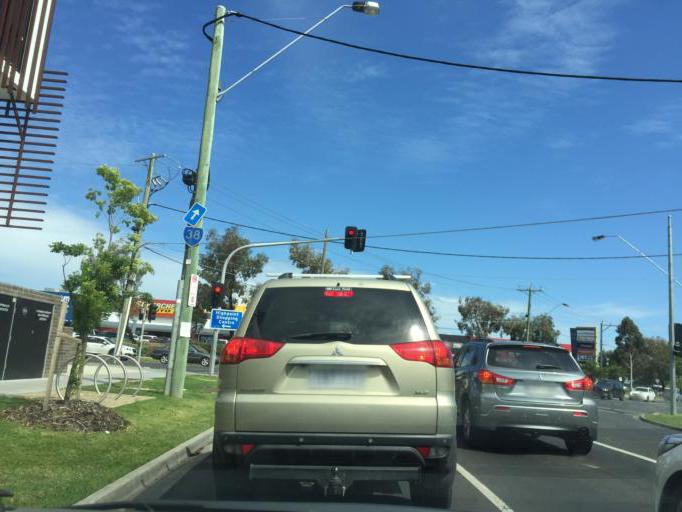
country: AU
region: Victoria
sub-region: Maribyrnong
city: Maribyrnong
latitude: -37.7747
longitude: 144.8813
